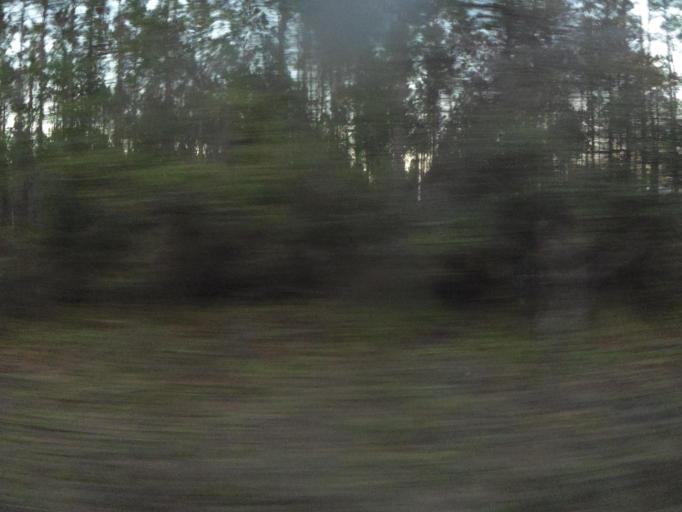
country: US
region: Florida
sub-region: Clay County
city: Asbury Lake
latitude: 29.9645
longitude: -81.7938
